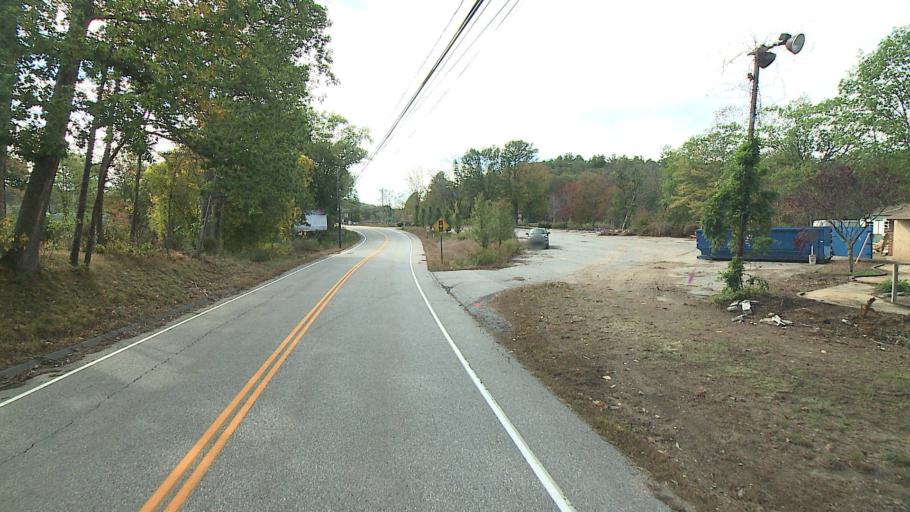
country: US
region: Connecticut
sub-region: Windham County
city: Thompson
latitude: 41.9490
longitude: -71.8876
